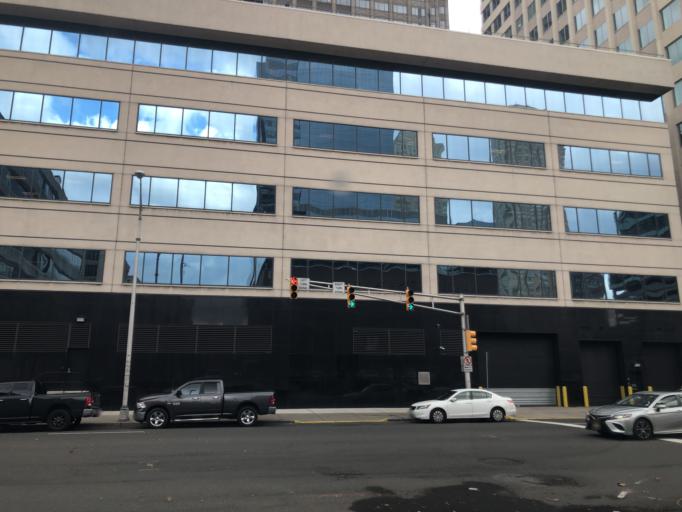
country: US
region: New Jersey
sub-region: Hudson County
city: Hoboken
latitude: 40.7174
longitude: -74.0347
